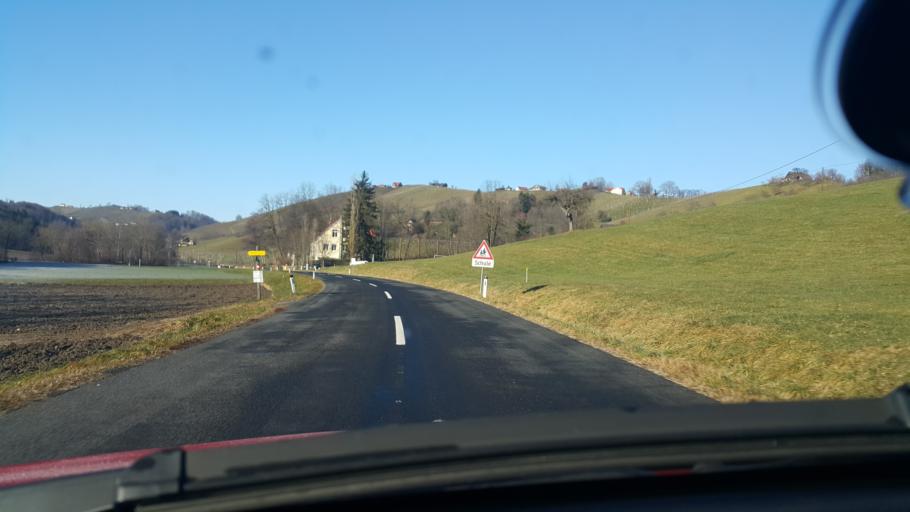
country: AT
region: Styria
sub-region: Politischer Bezirk Leibnitz
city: Sulztal an der Weinstrasse
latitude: 46.6491
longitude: 15.5458
